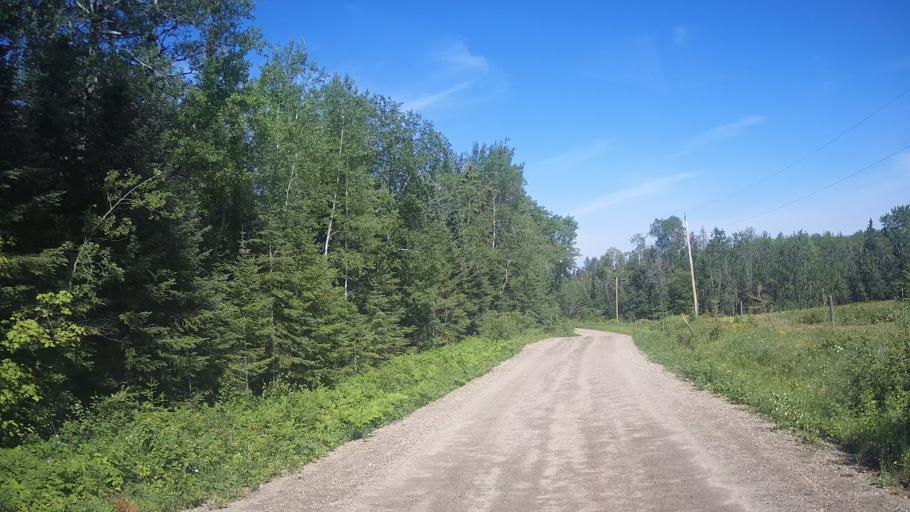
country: CA
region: Ontario
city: Dryden
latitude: 49.8165
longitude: -93.3298
